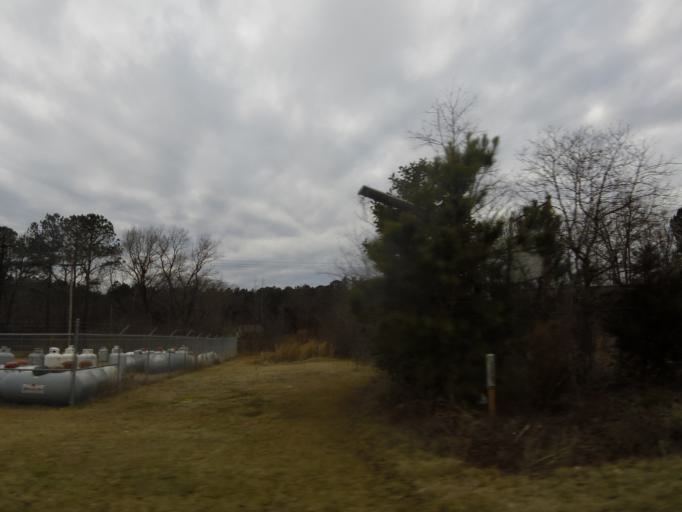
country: US
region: North Carolina
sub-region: Halifax County
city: Scotland Neck
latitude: 36.1538
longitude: -77.4119
